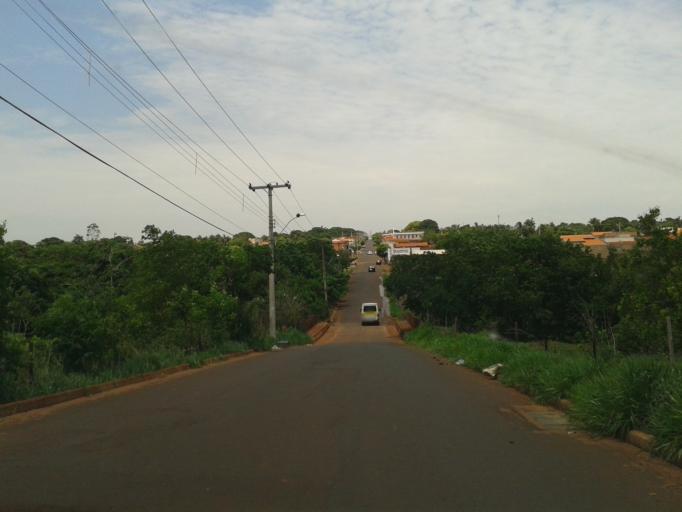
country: BR
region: Minas Gerais
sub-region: Ituiutaba
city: Ituiutaba
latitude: -18.9914
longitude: -49.4408
